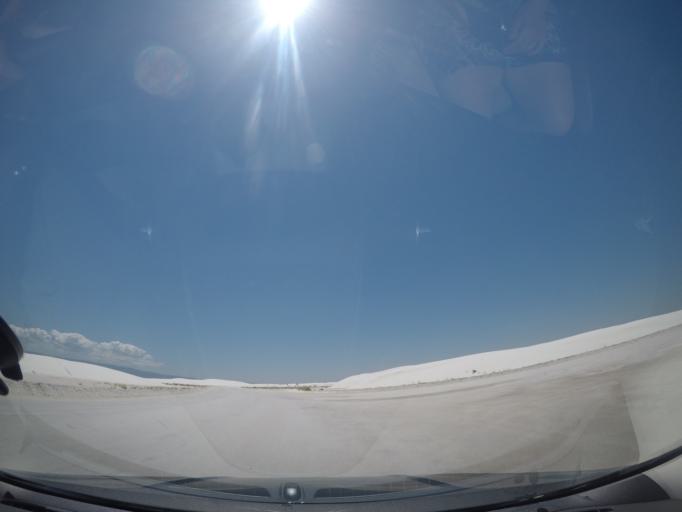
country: US
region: New Mexico
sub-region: Otero County
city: Holloman Air Force Base
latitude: 32.8123
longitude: -106.2658
